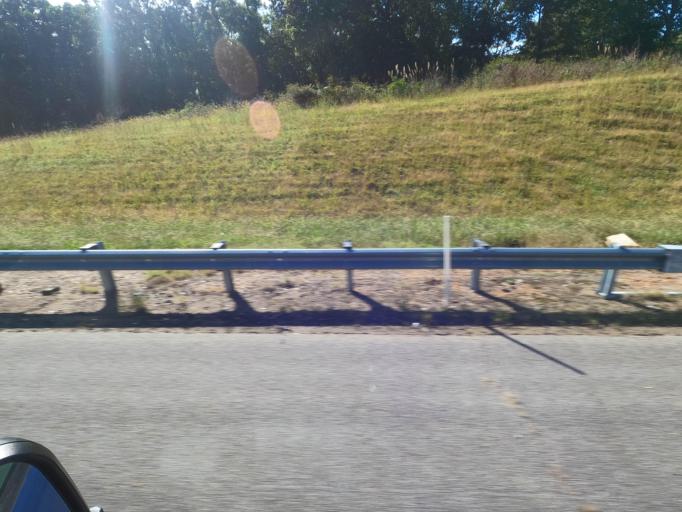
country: US
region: Tennessee
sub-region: Shelby County
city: Lakeland
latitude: 35.3106
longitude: -89.7419
